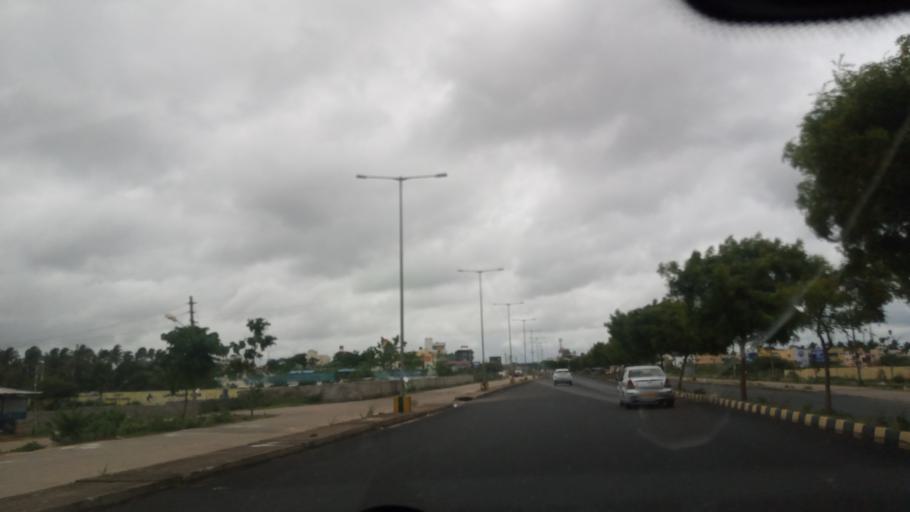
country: IN
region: Karnataka
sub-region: Mysore
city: Mysore
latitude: 12.3265
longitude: 76.5969
